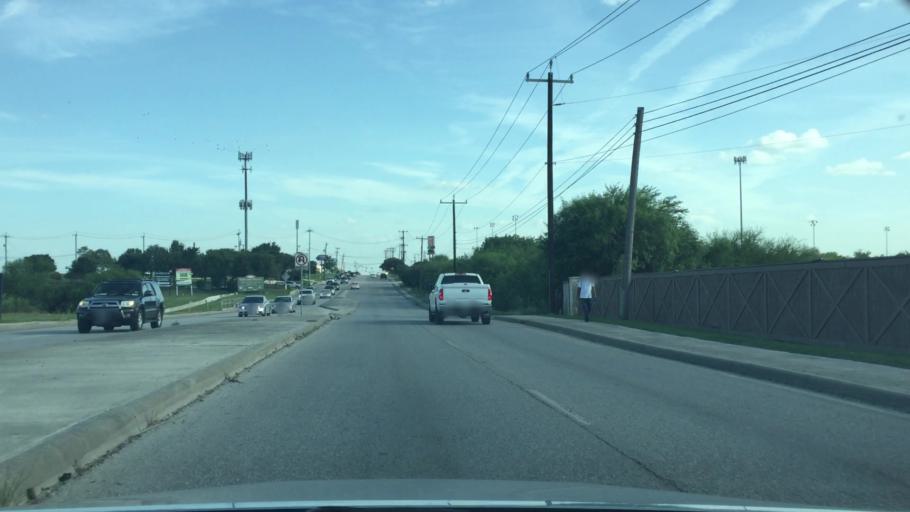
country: US
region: Texas
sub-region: Bexar County
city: Kirby
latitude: 29.4511
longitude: -98.3608
